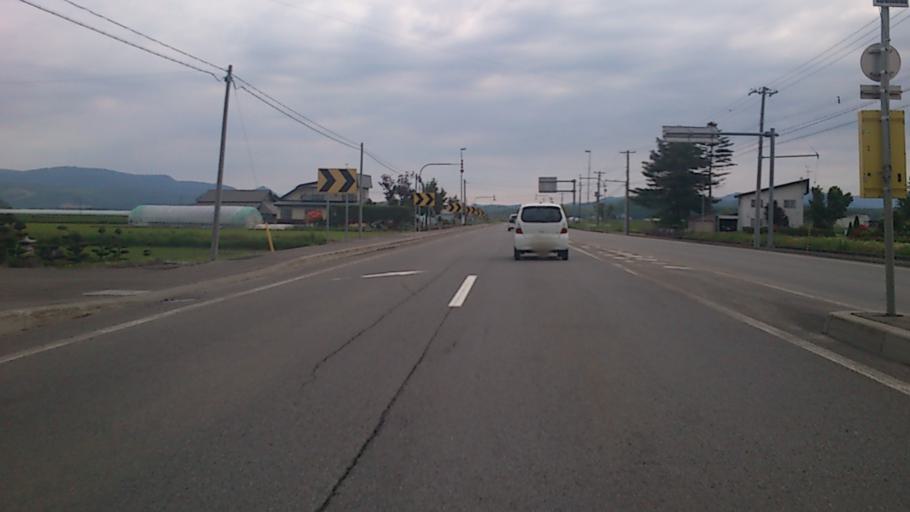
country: JP
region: Hokkaido
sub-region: Asahikawa-shi
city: Asahikawa
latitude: 43.8561
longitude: 142.5067
